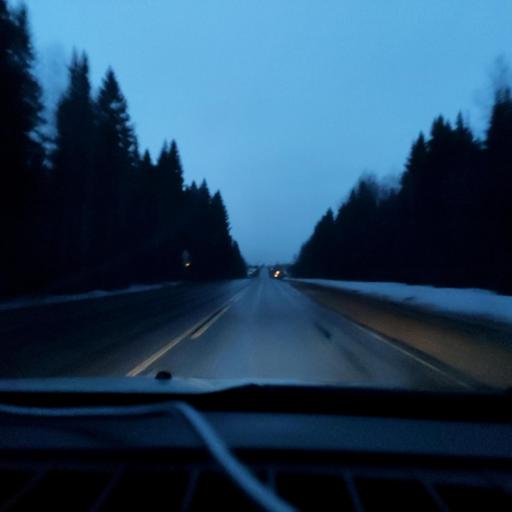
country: RU
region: Perm
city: Ust'-Kachka
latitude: 57.9222
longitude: 55.7636
